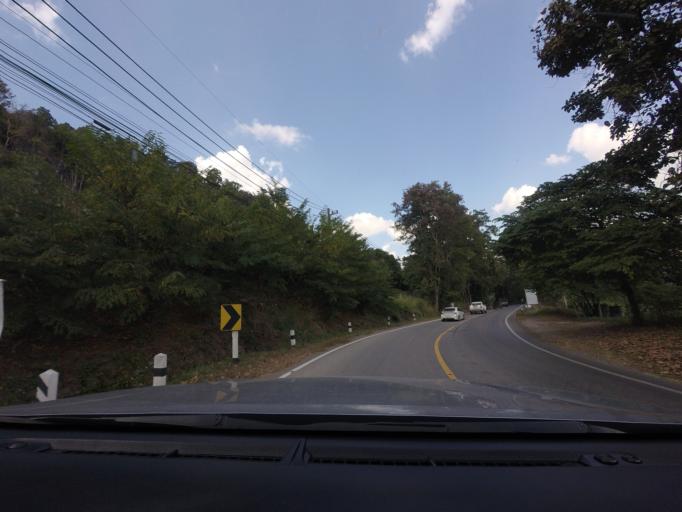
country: TH
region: Chiang Mai
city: Chai Prakan
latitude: 19.6126
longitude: 99.1264
